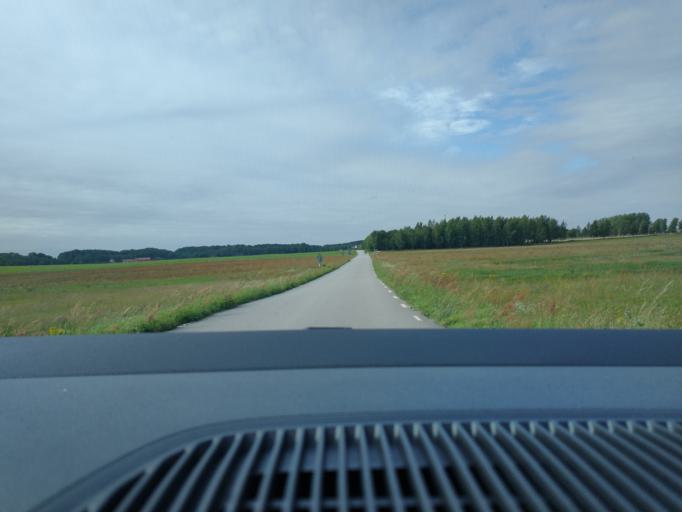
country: SE
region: Skane
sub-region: Lunds Kommun
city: Veberod
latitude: 55.6725
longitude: 13.4381
